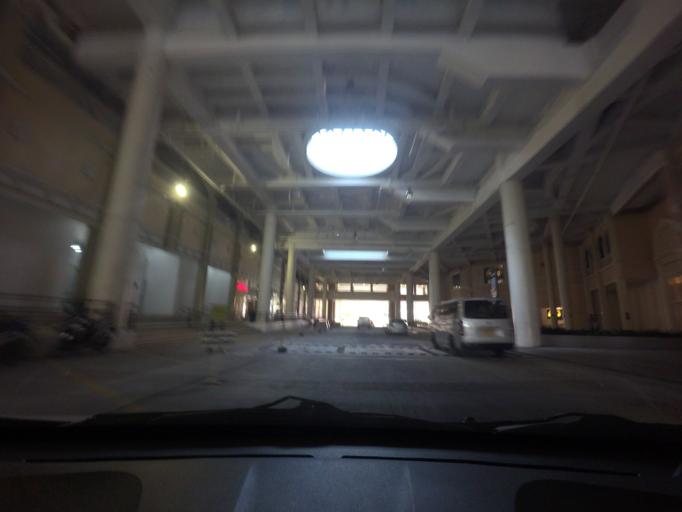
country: PH
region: Calabarzon
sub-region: Province of Rizal
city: Pateros
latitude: 14.5336
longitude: 121.0514
